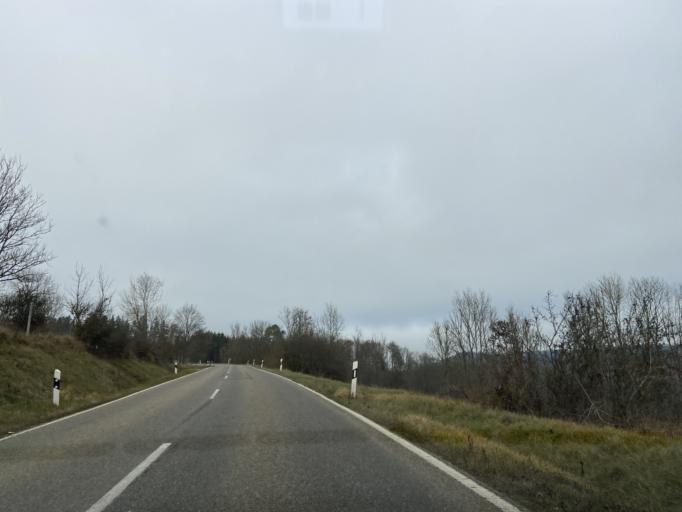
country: DE
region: Baden-Wuerttemberg
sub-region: Tuebingen Region
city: Gammertingen
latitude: 48.2489
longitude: 9.2089
